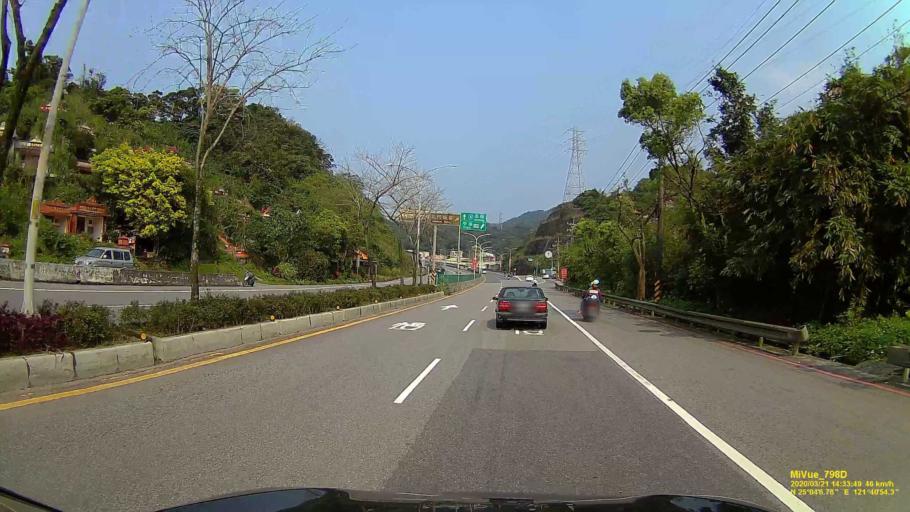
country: TW
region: Taiwan
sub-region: Keelung
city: Keelung
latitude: 25.0686
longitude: 121.6820
